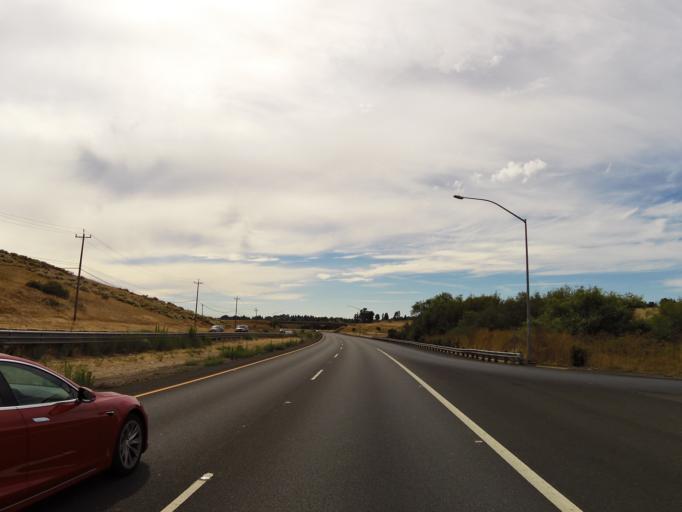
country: US
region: California
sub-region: Contra Costa County
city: Rodeo
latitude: 38.0147
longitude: -122.2405
